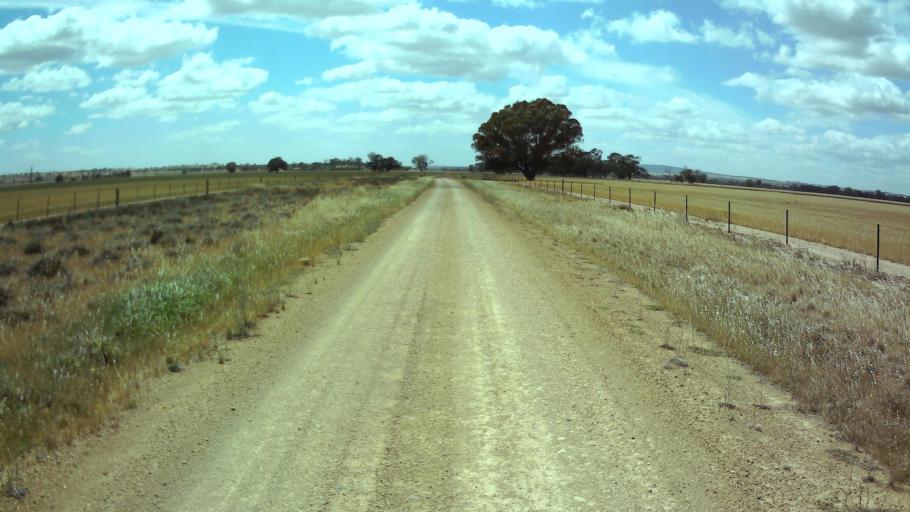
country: AU
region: New South Wales
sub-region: Weddin
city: Grenfell
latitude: -33.9964
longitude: 148.2906
